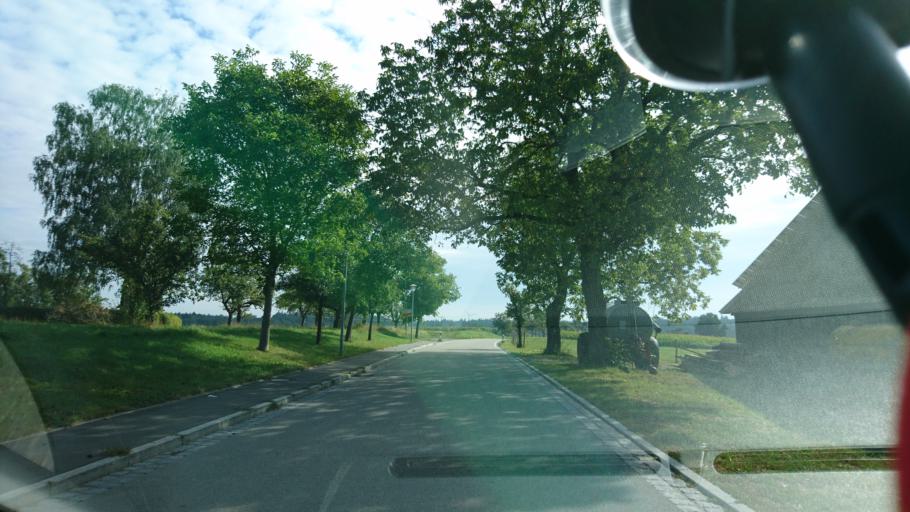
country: DE
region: Baden-Wuerttemberg
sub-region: Regierungsbezirk Stuttgart
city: Mainhardt
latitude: 49.0899
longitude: 9.5785
